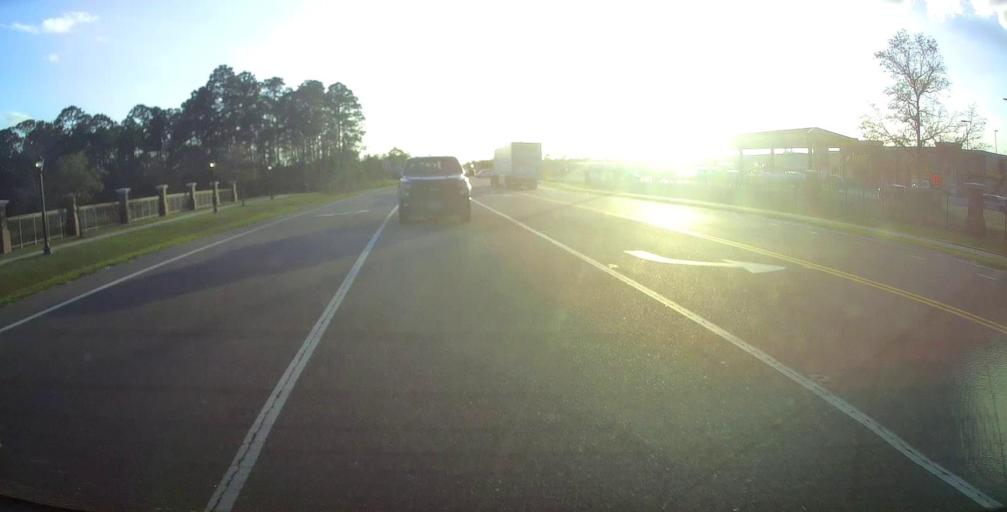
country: US
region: Georgia
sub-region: Chatham County
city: Bloomingdale
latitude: 32.1839
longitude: -81.4547
